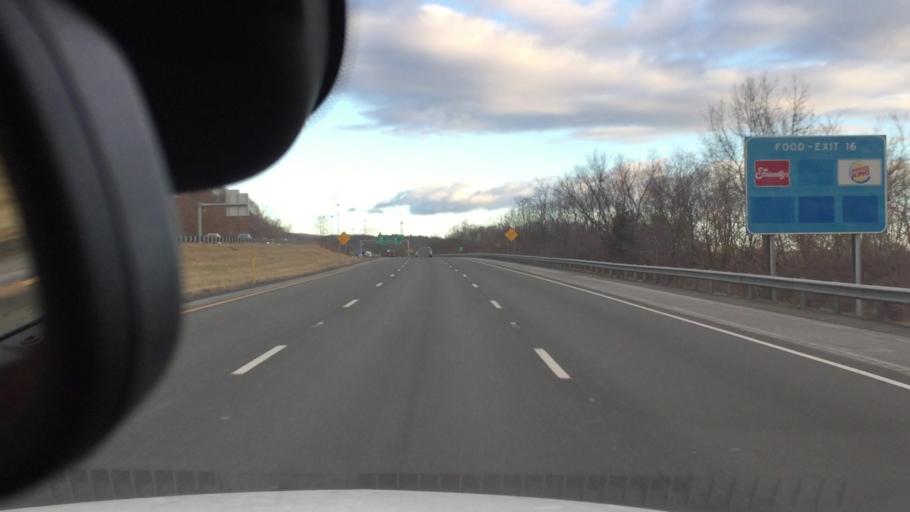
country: US
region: Massachusetts
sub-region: Hampden County
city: Holyoke
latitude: 42.1922
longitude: -72.6378
